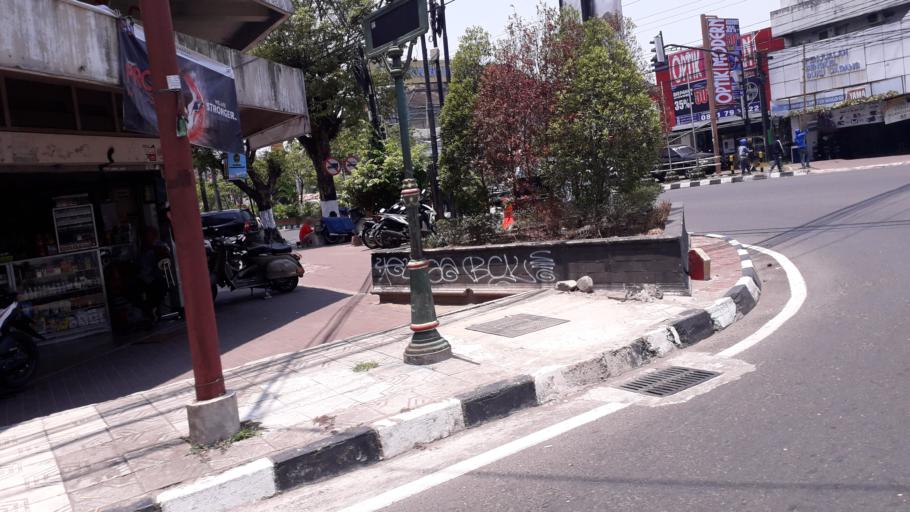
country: ID
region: Daerah Istimewa Yogyakarta
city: Yogyakarta
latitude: -7.7826
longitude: 110.3609
